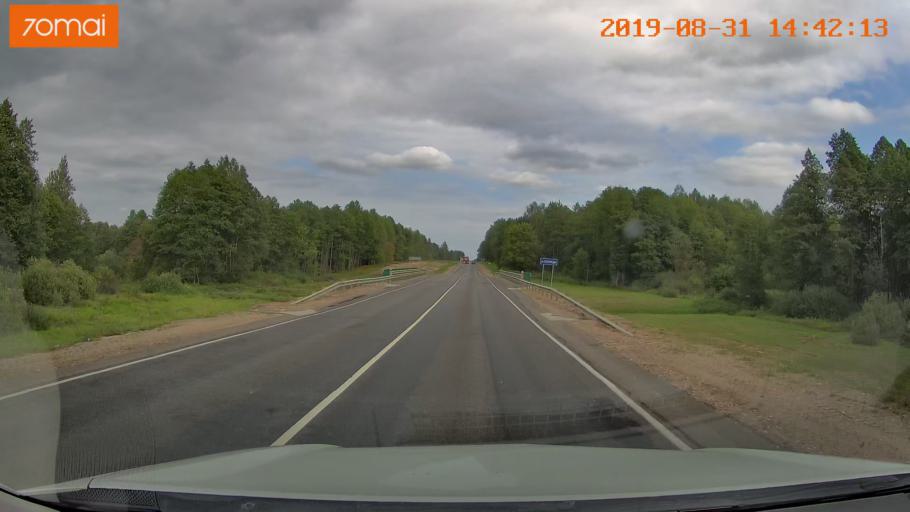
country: RU
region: Smolensk
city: Yekimovichi
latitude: 54.2067
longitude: 33.6036
